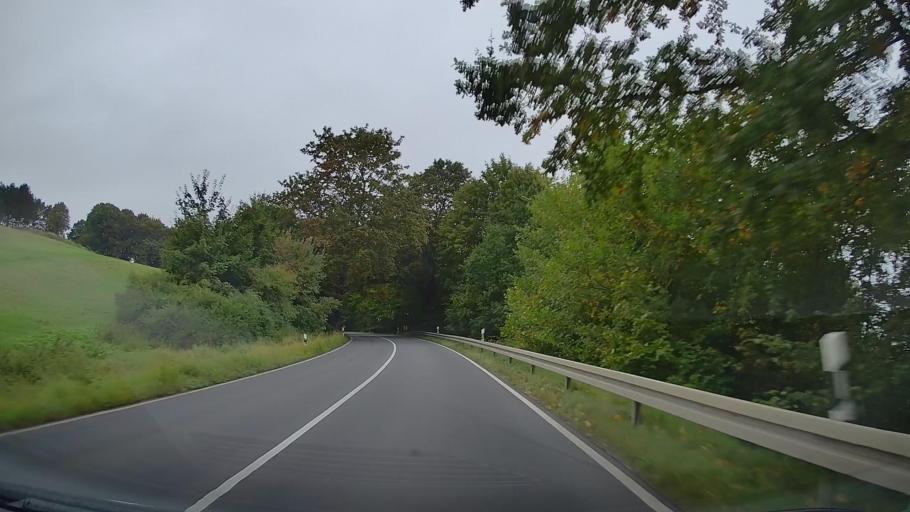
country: DE
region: Mecklenburg-Vorpommern
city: Sternberg
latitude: 53.7055
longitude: 11.8400
